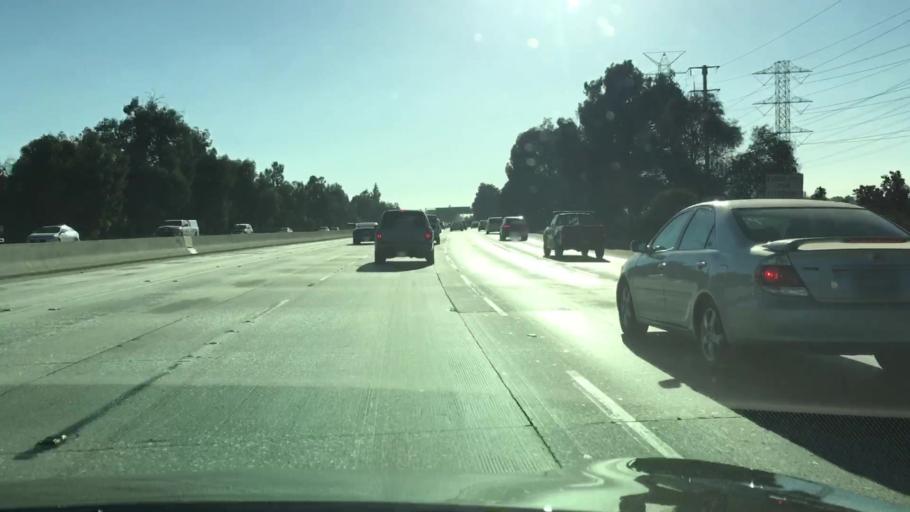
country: US
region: California
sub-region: Los Angeles County
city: Avocado Heights
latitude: 34.0416
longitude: -118.0137
